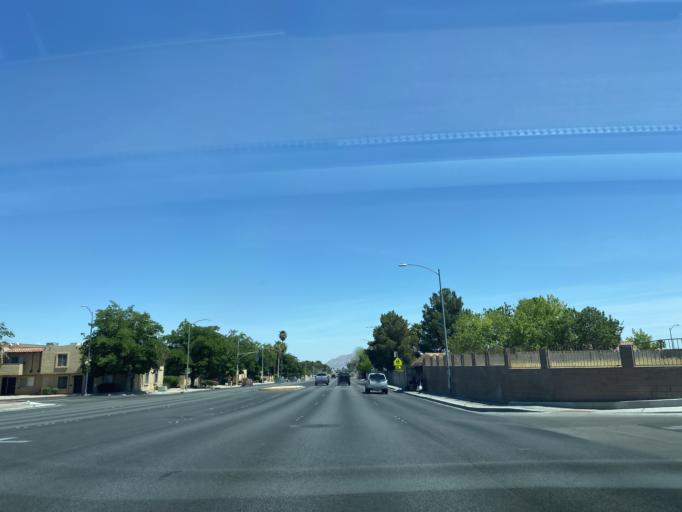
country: US
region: Nevada
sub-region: Clark County
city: Las Vegas
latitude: 36.1956
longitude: -115.2202
